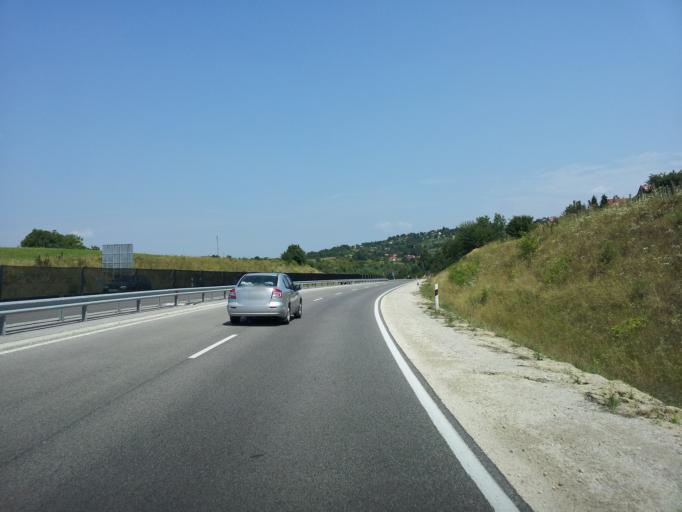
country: HU
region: Zala
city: Zalaegerszeg
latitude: 46.8369
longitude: 16.8851
